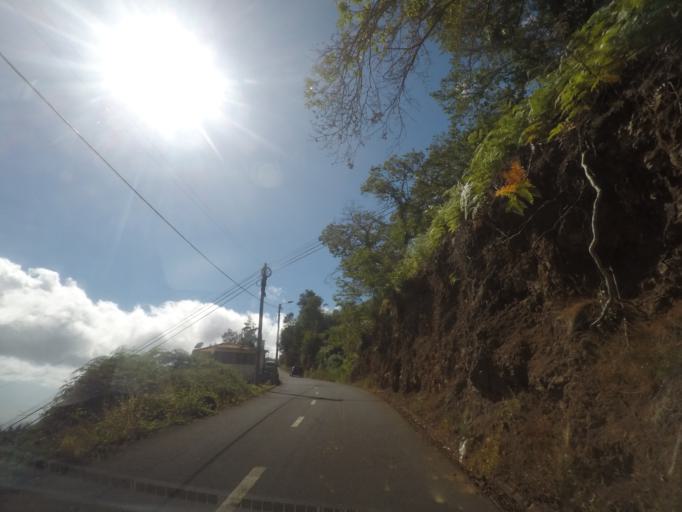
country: PT
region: Madeira
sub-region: Ribeira Brava
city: Campanario
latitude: 32.6916
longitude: -17.0311
